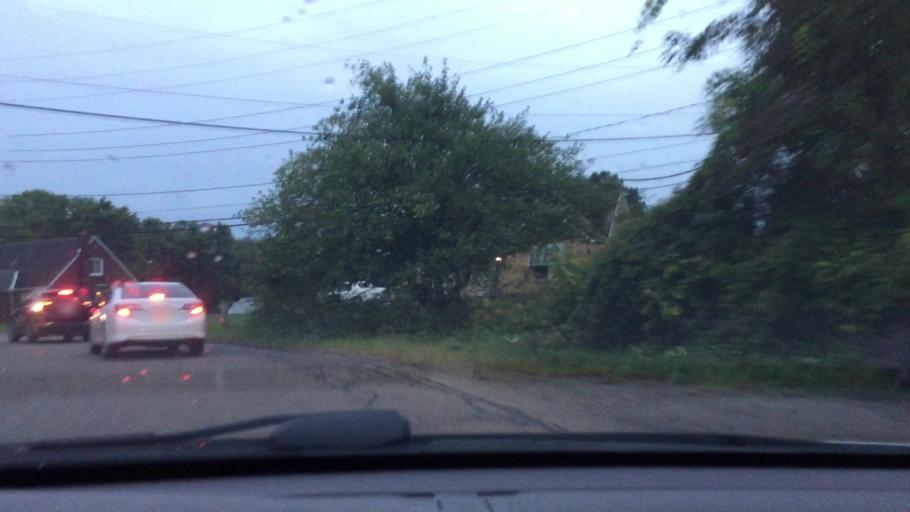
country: US
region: Pennsylvania
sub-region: Allegheny County
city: Cheswick
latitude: 40.5566
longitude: -79.8233
